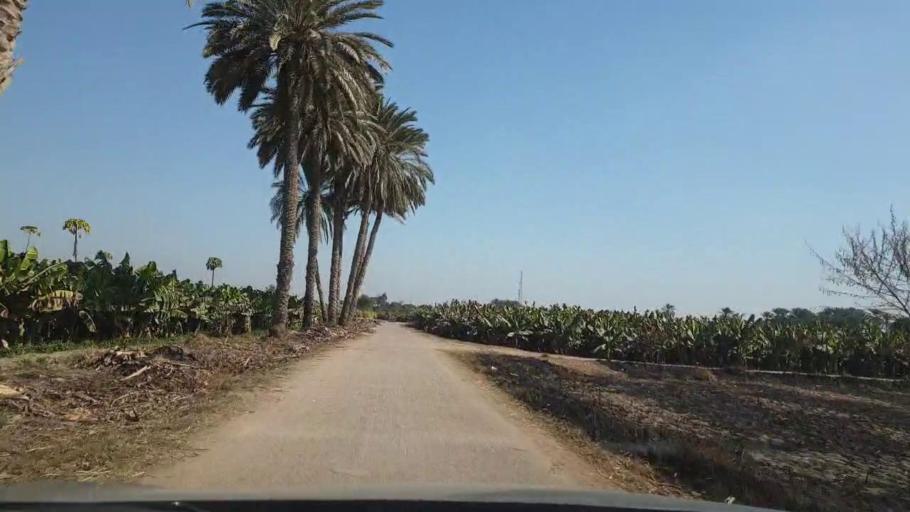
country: PK
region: Sindh
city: Tando Adam
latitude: 25.6371
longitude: 68.6768
